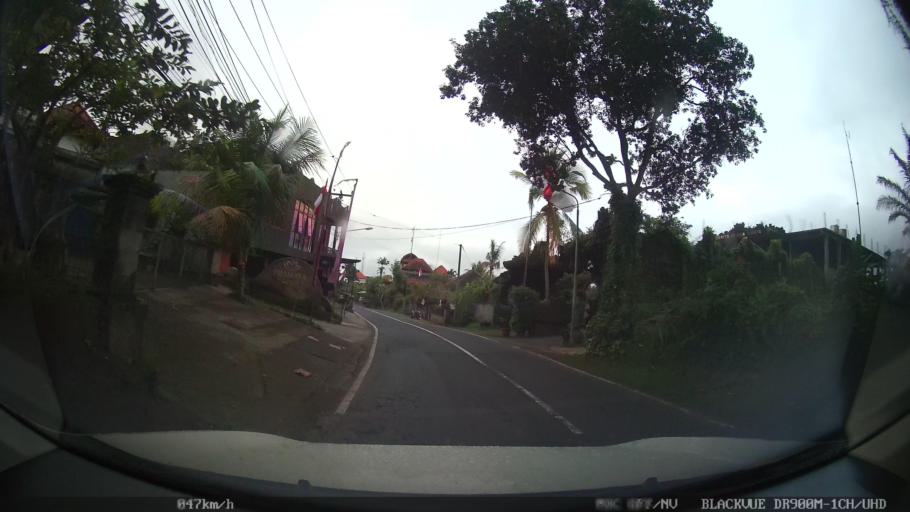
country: ID
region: Bali
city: Badung
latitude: -8.4151
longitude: 115.2440
